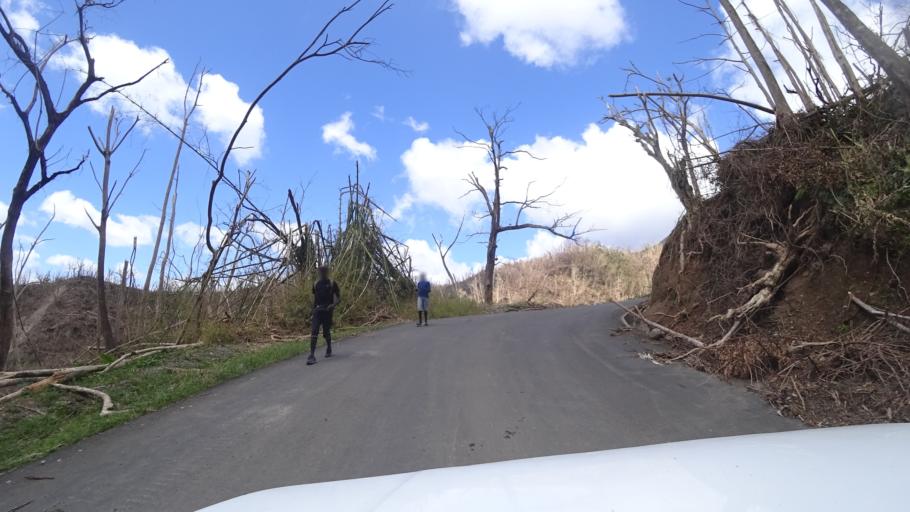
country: DM
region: Saint Luke
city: Pointe Michel
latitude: 15.2736
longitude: -61.3581
